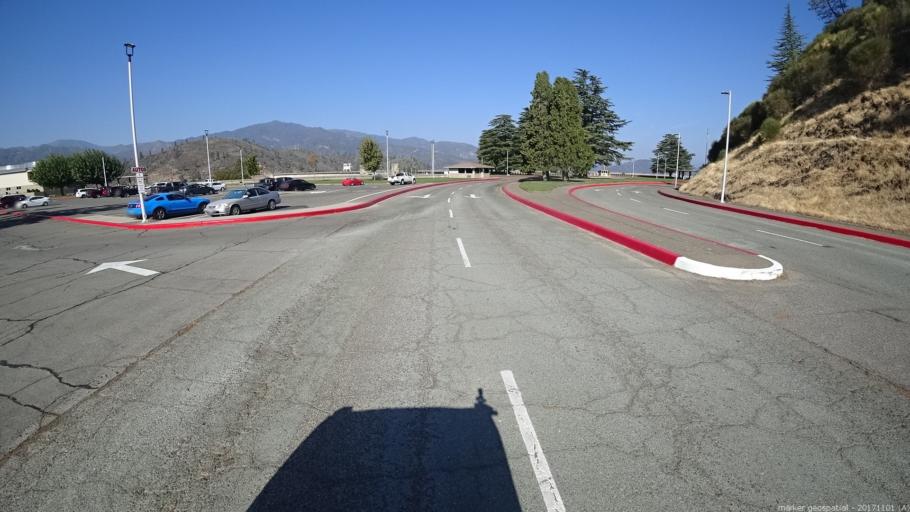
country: US
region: California
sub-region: Shasta County
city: Central Valley (historical)
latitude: 40.7135
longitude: -122.4160
